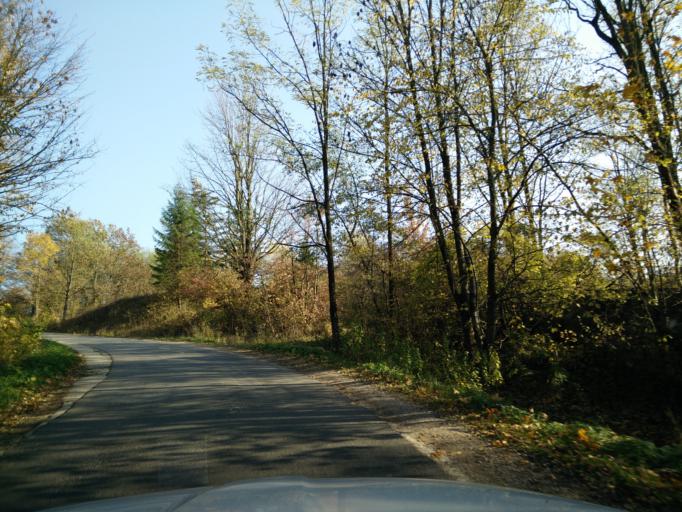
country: SK
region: Zilinsky
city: Rajec
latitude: 49.0868
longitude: 18.6468
